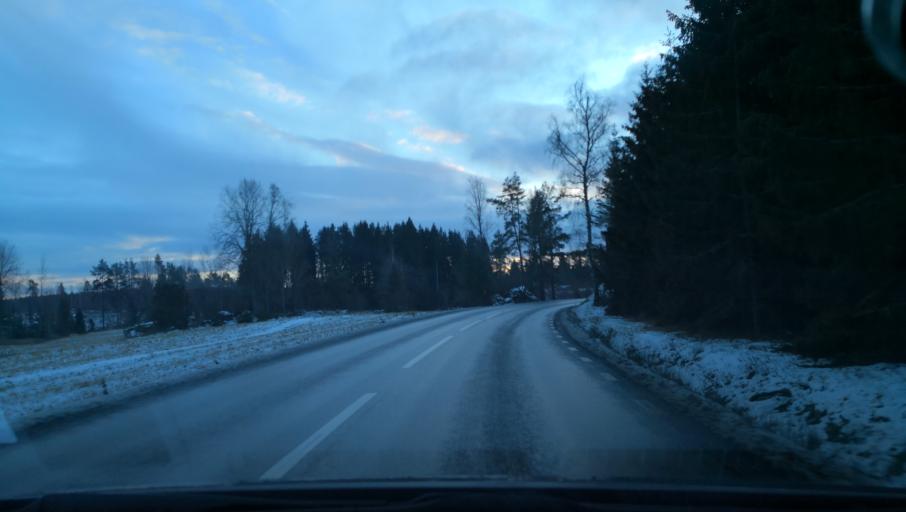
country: SE
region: Soedermanland
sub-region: Katrineholms Kommun
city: Katrineholm
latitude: 59.1874
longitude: 16.2526
